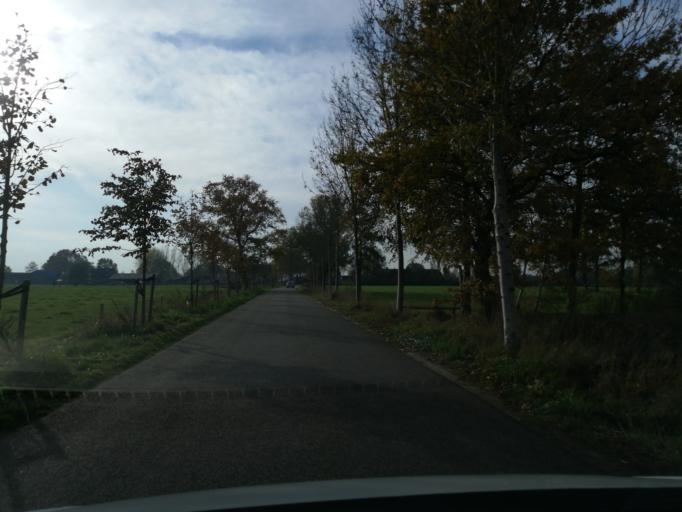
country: NL
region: Gelderland
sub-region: Gemeente Apeldoorn
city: Apeldoorn
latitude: 52.2468
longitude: 6.0306
